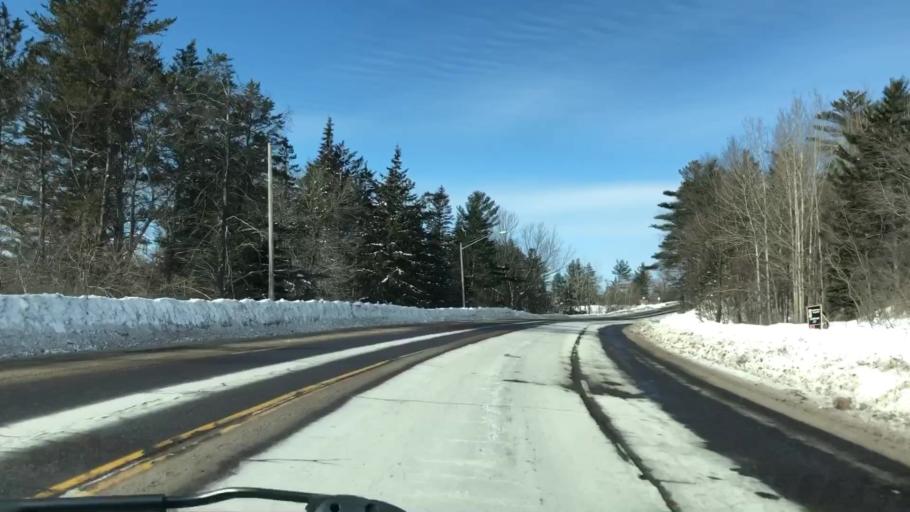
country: US
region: Minnesota
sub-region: Saint Louis County
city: Arnold
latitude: 46.8387
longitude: -92.0796
